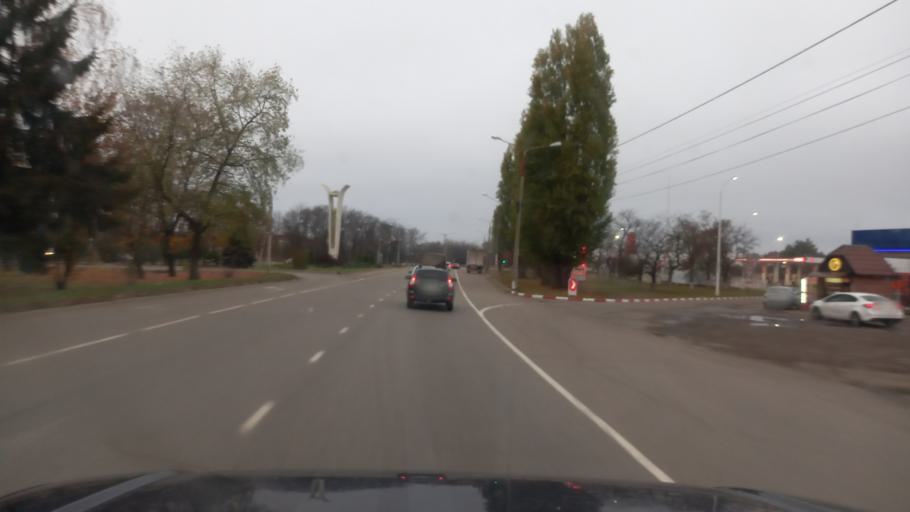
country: RU
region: Adygeya
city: Maykop
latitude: 44.6232
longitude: 40.0565
